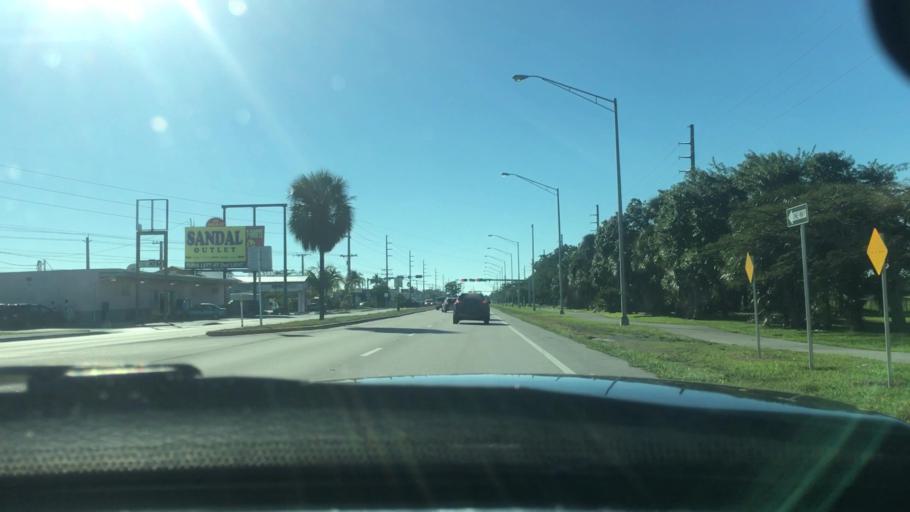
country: US
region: Florida
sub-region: Monroe County
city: Stock Island
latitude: 24.5736
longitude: -81.7409
